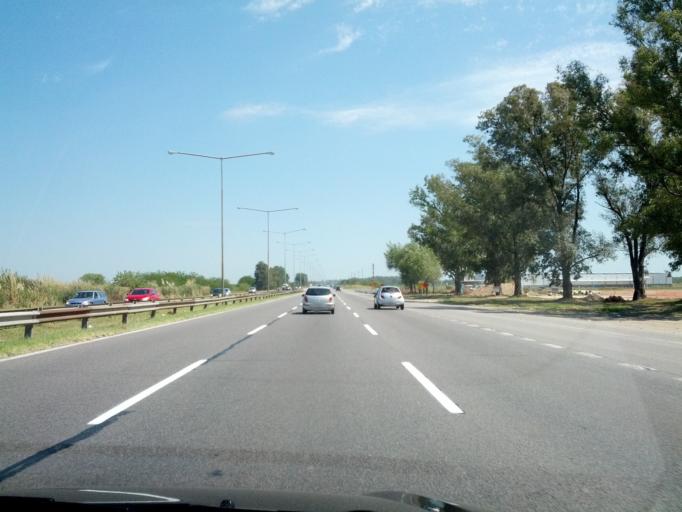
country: AR
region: Buenos Aires
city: Belen de Escobar
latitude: -34.3153
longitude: -58.8697
